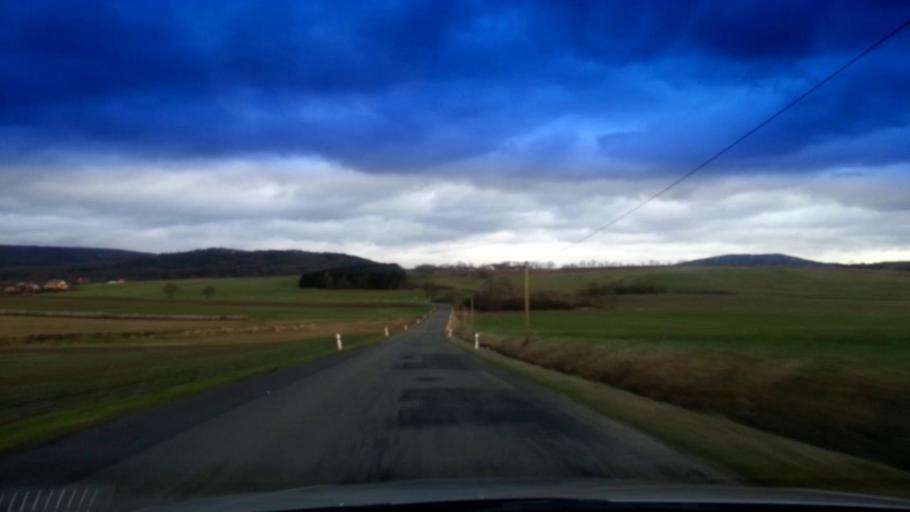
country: DE
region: Bavaria
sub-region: Upper Franconia
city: Schesslitz
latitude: 49.9978
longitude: 11.0083
